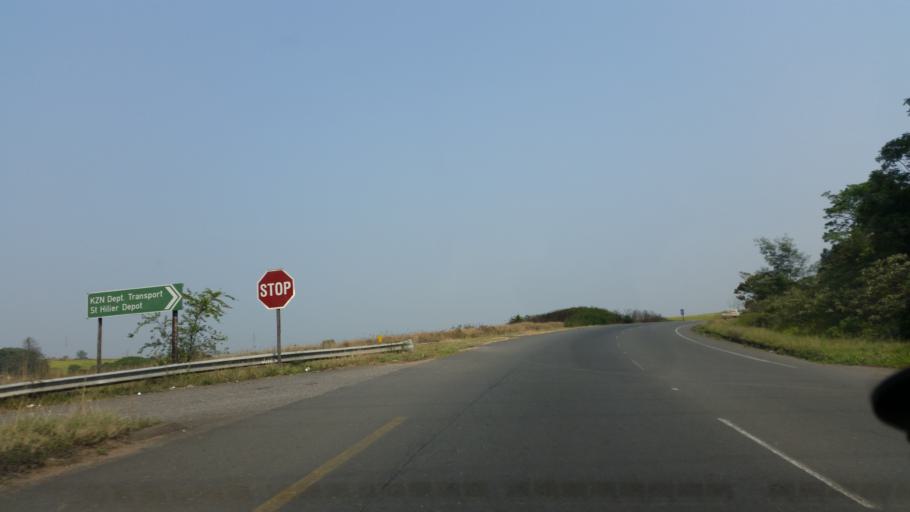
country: ZA
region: KwaZulu-Natal
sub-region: eThekwini Metropolitan Municipality
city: Mpumalanga
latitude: -29.8026
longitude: 30.7701
